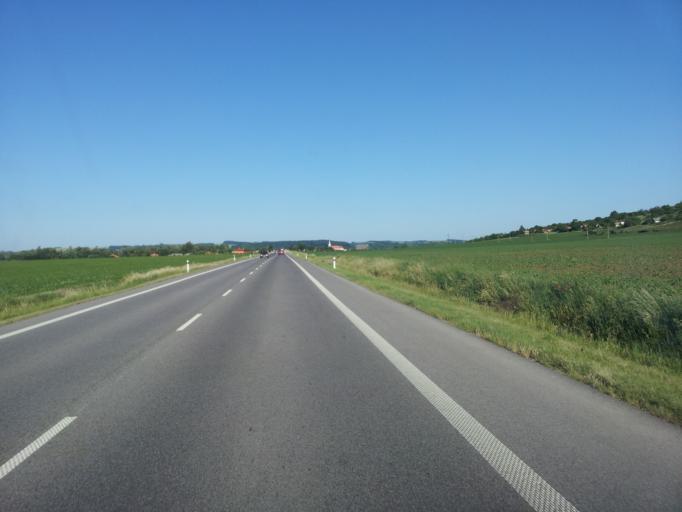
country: SK
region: Nitriansky
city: Sahy
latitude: 48.0853
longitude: 18.9200
